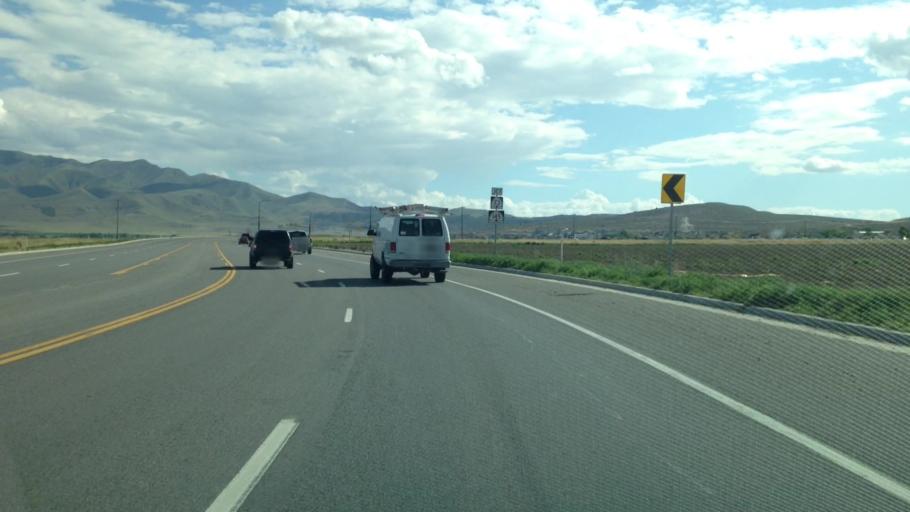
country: US
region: Utah
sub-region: Utah County
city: Saratoga Springs
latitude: 40.3869
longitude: -111.9290
